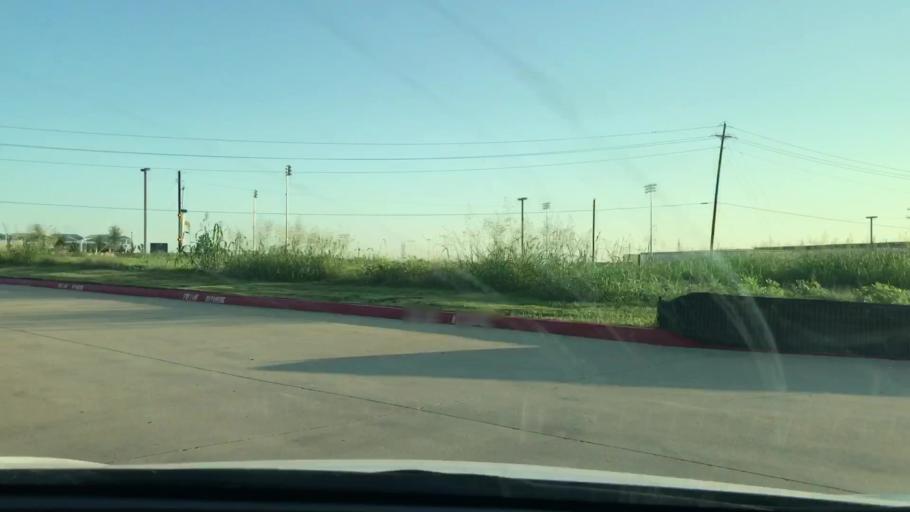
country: US
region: Texas
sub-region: Dallas County
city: Coppell
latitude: 32.9248
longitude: -96.9845
